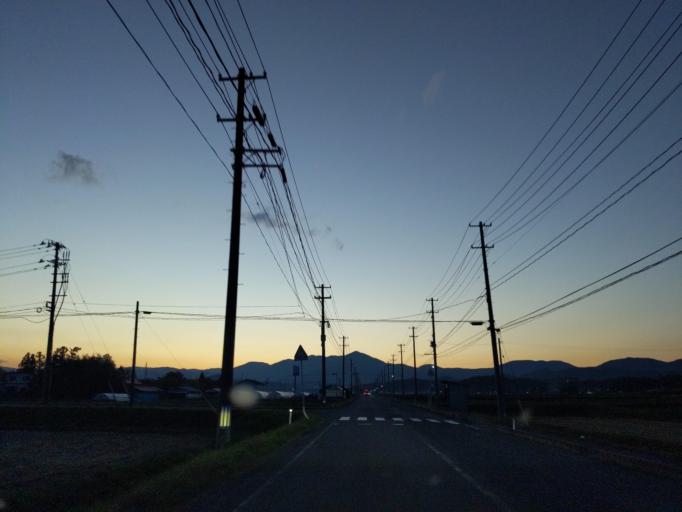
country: JP
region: Fukushima
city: Koriyama
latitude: 37.4551
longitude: 140.3198
